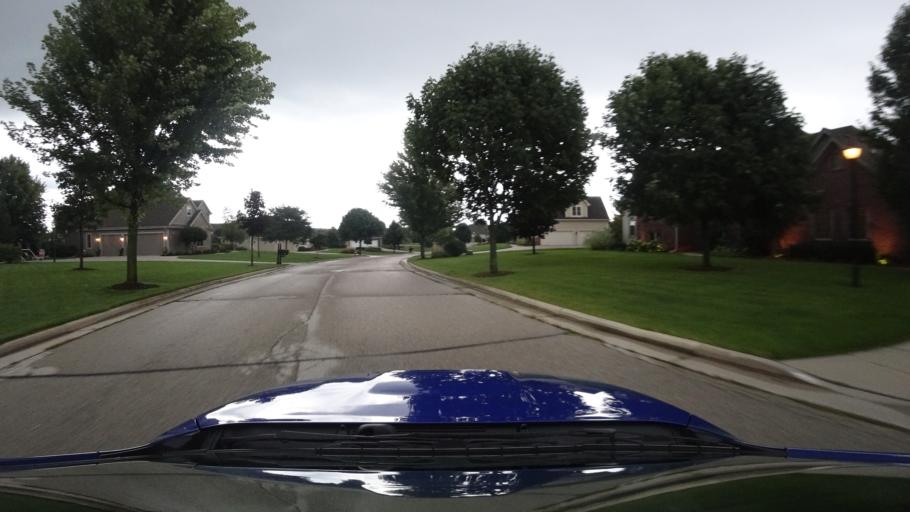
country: US
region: Wisconsin
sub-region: Waukesha County
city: Hartland
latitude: 43.1210
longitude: -88.3383
